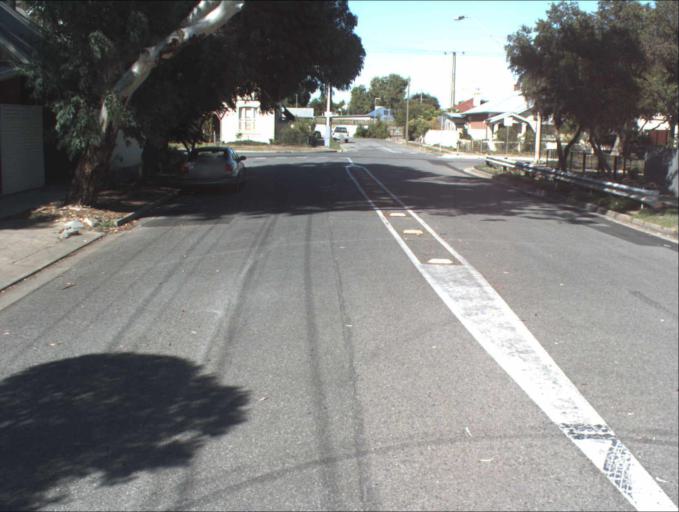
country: AU
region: South Australia
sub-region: Port Adelaide Enfield
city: Alberton
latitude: -34.8566
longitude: 138.5188
